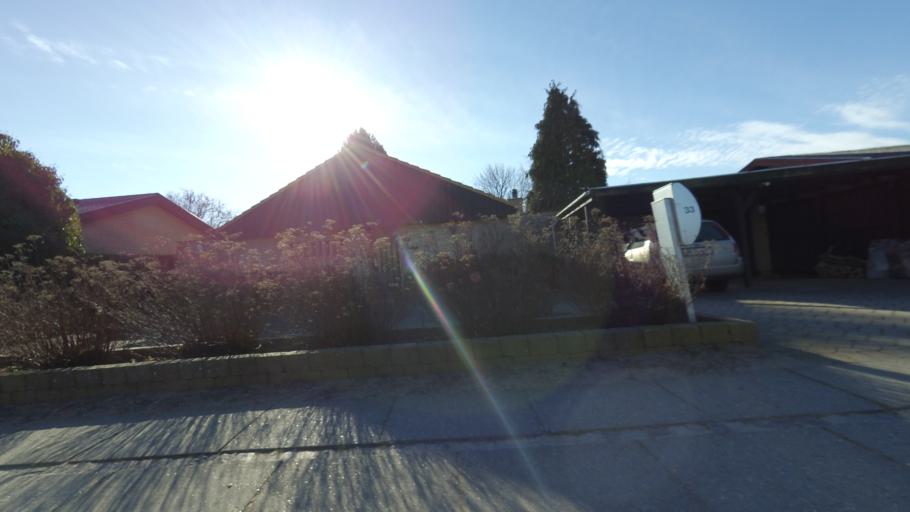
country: DK
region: Central Jutland
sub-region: Arhus Kommune
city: Kolt
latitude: 56.1071
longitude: 10.0949
